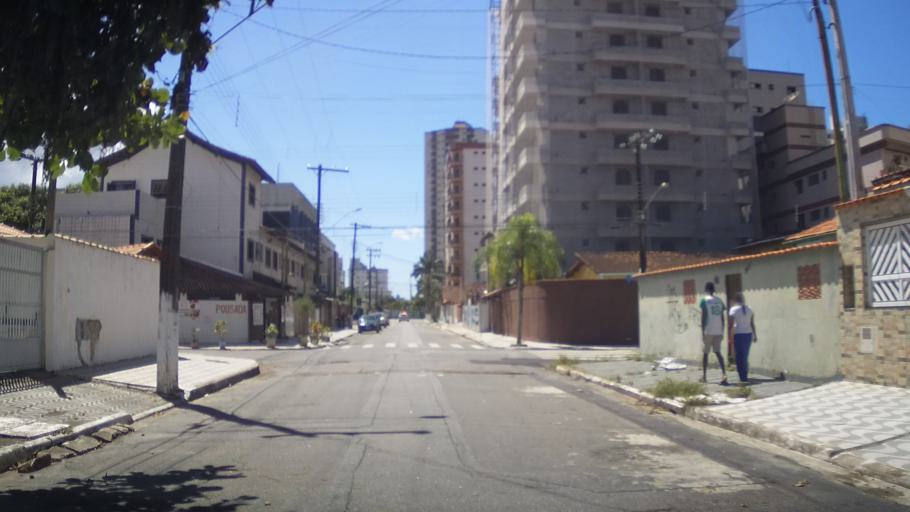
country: BR
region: Sao Paulo
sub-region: Mongagua
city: Mongagua
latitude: -24.0499
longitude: -46.5305
